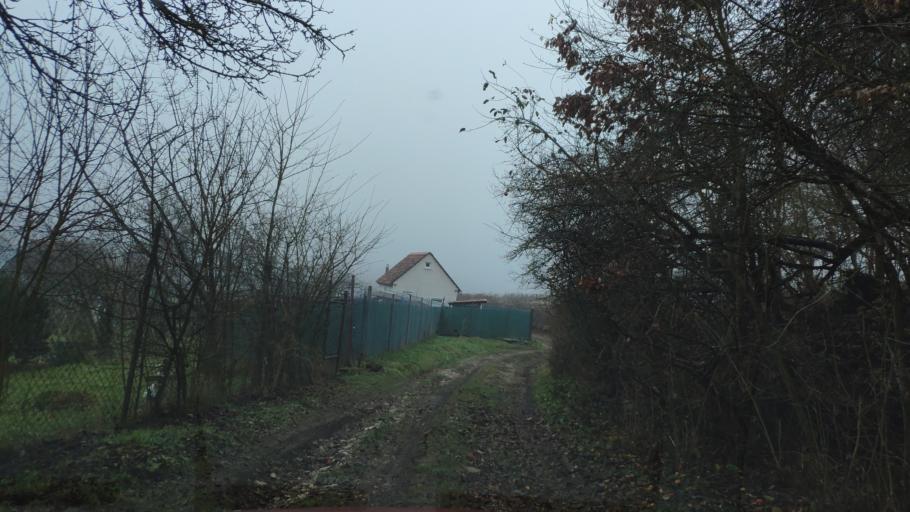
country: SK
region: Banskobystricky
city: Revuca
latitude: 48.6528
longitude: 20.2575
